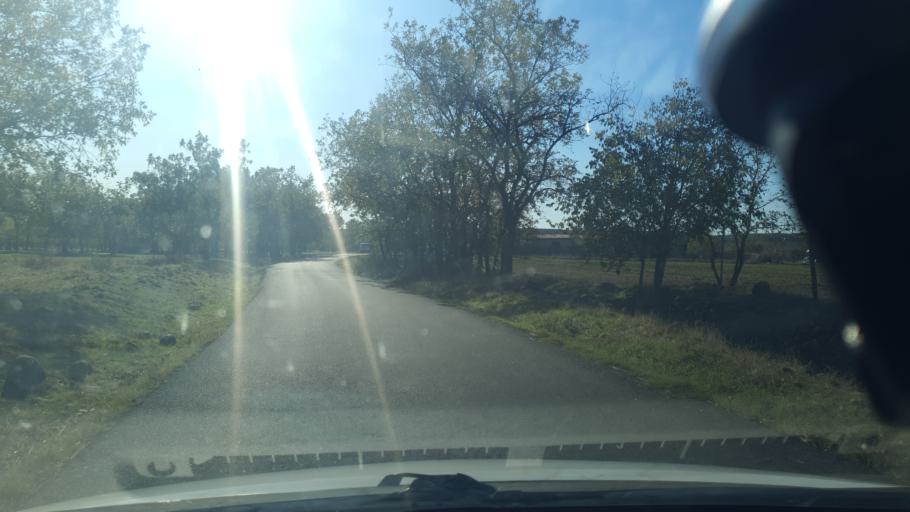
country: ES
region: Castille and Leon
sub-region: Provincia de Avila
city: Candeleda
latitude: 40.1225
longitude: -5.2664
